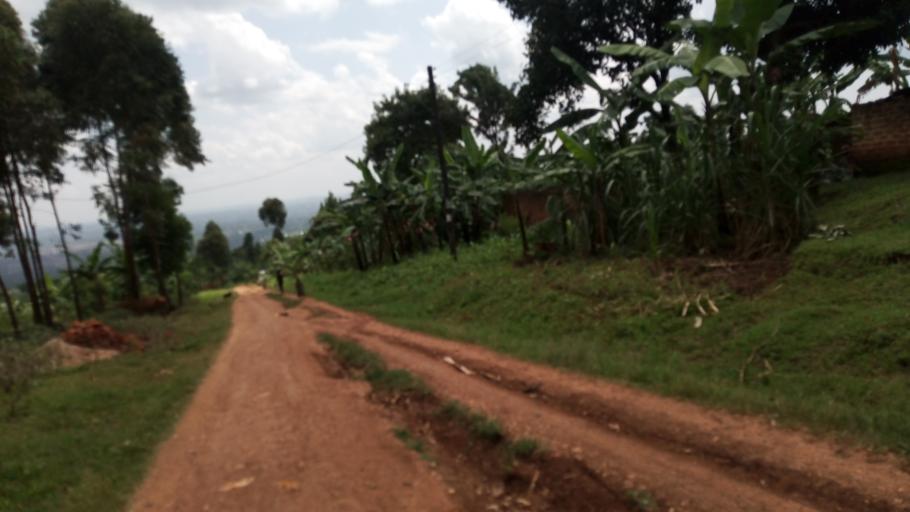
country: UG
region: Eastern Region
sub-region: Mbale District
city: Mbale
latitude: 1.0559
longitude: 34.2193
